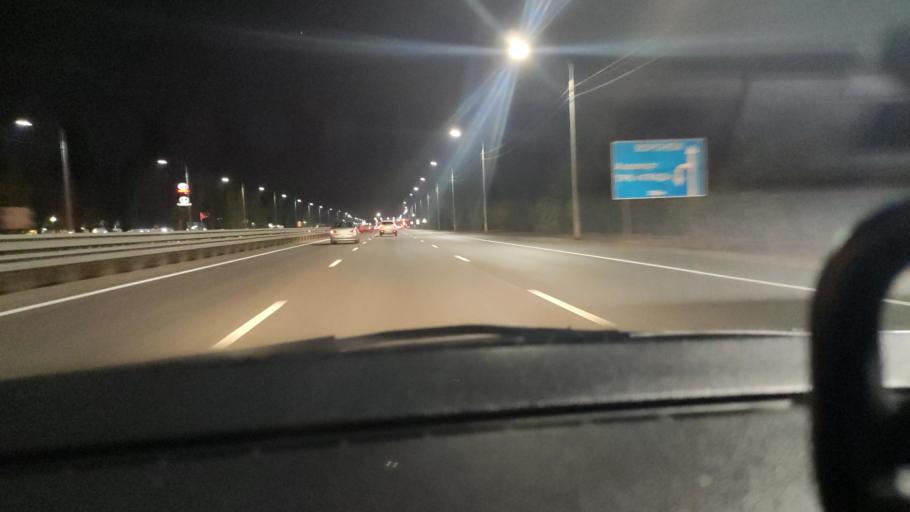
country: RU
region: Voronezj
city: Podgornoye
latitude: 51.7814
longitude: 39.1958
